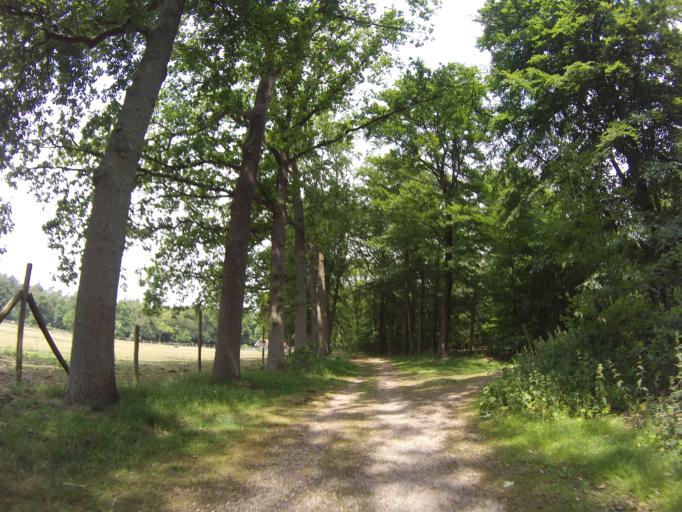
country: NL
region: Utrecht
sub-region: Gemeente Utrechtse Heuvelrug
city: Driebergen-Rijsenburg
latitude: 52.0884
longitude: 5.3047
